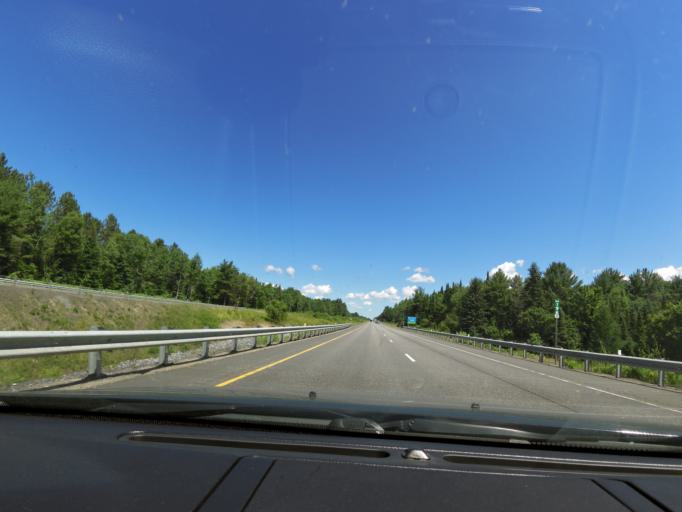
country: CA
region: Ontario
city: Bracebridge
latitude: 45.1161
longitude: -79.3106
